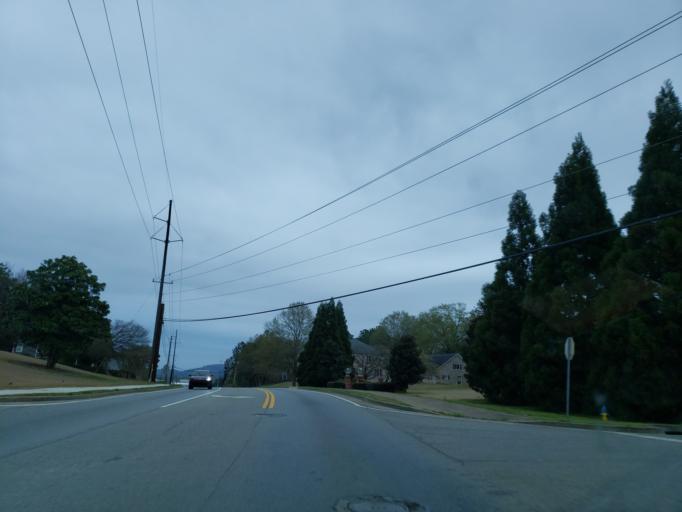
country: US
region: Georgia
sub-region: Bartow County
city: Cartersville
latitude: 34.1496
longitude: -84.8070
